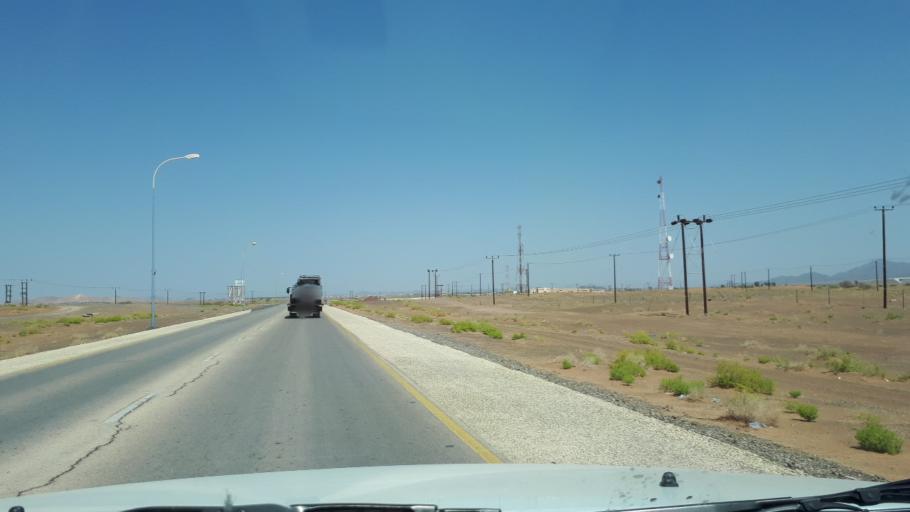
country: OM
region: Ash Sharqiyah
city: Al Qabil
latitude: 22.5078
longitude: 58.7434
